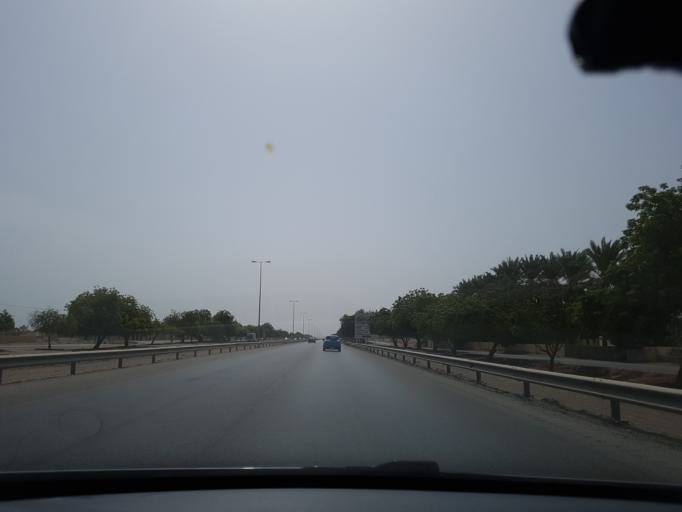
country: OM
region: Al Batinah
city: As Suwayq
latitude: 23.8417
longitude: 57.3706
